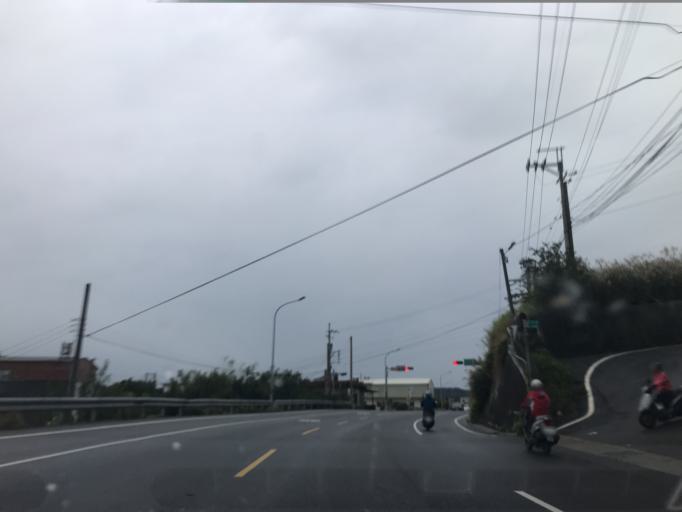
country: TW
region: Taiwan
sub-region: Hsinchu
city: Zhubei
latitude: 24.8358
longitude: 121.0953
